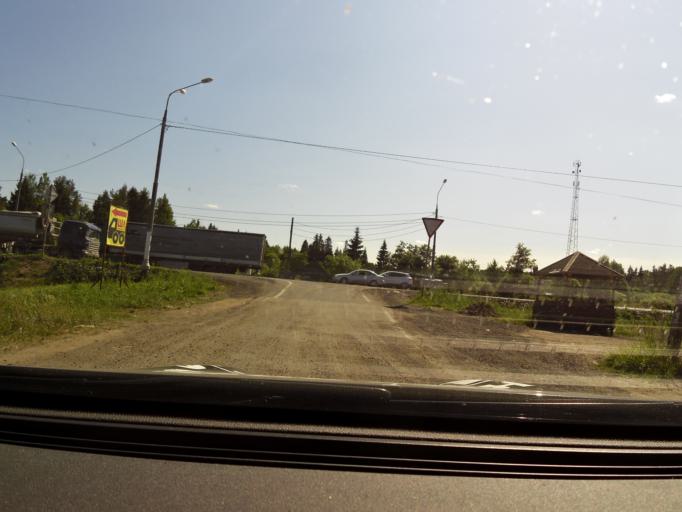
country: RU
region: Novgorod
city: Proletariy
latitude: 58.3855
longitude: 31.9818
